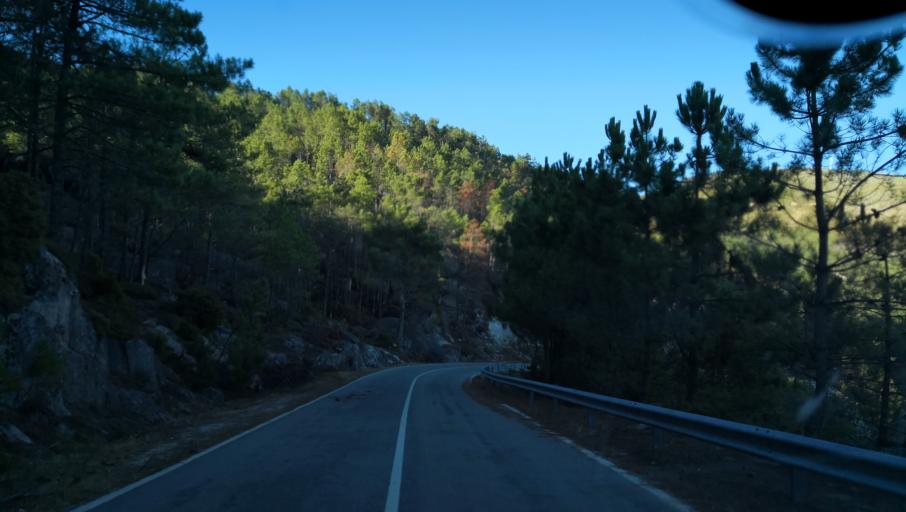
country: PT
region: Vila Real
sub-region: Vila Real
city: Vila Real
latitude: 41.3343
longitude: -7.7851
